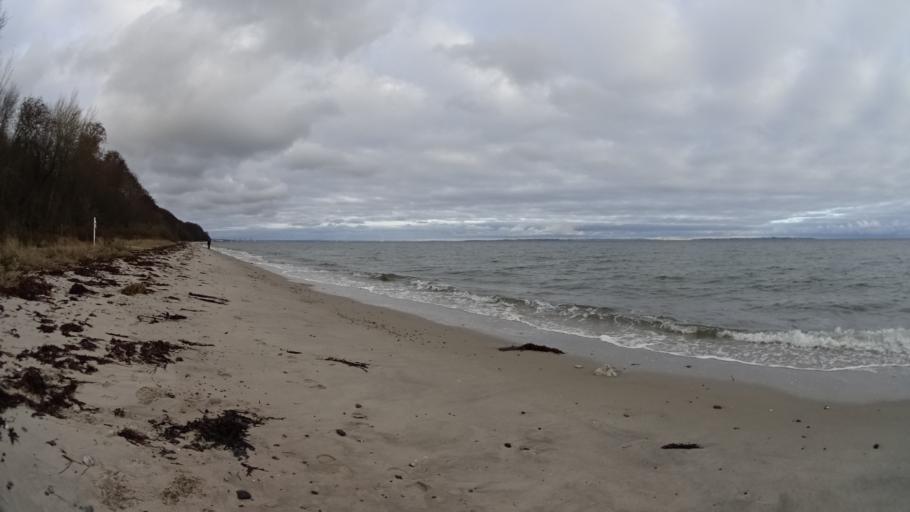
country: DK
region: Central Jutland
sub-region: Arhus Kommune
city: Beder
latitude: 56.0594
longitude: 10.2606
